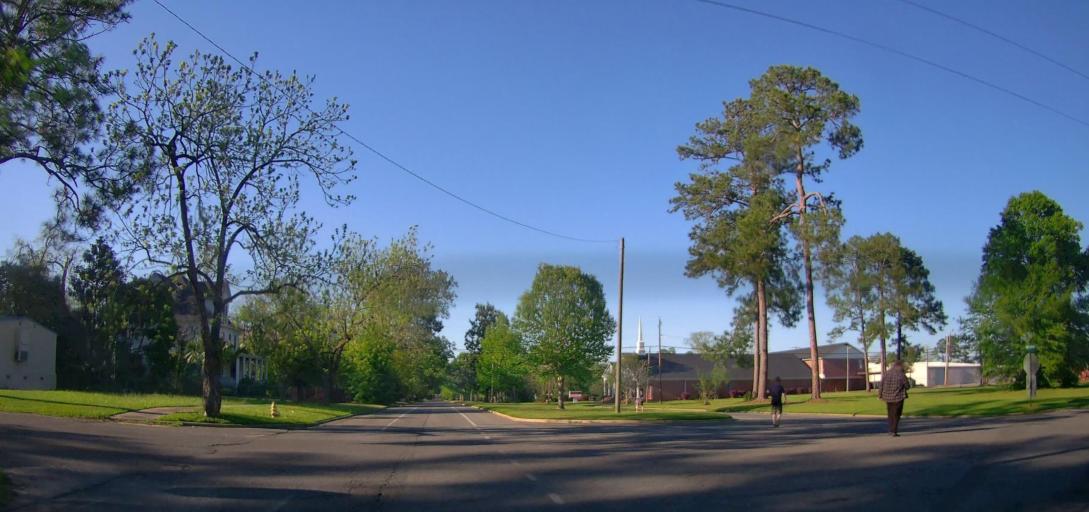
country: US
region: Georgia
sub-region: Ben Hill County
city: Fitzgerald
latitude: 31.7173
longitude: -83.2545
